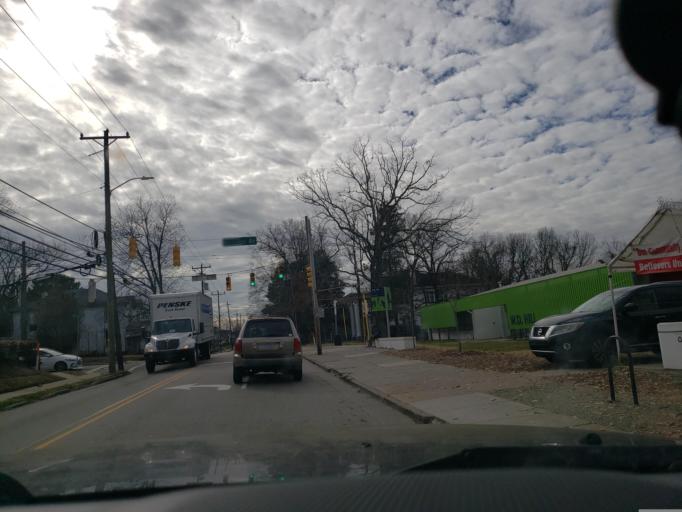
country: US
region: North Carolina
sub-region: Durham County
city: Durham
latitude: 35.9823
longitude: -78.8991
